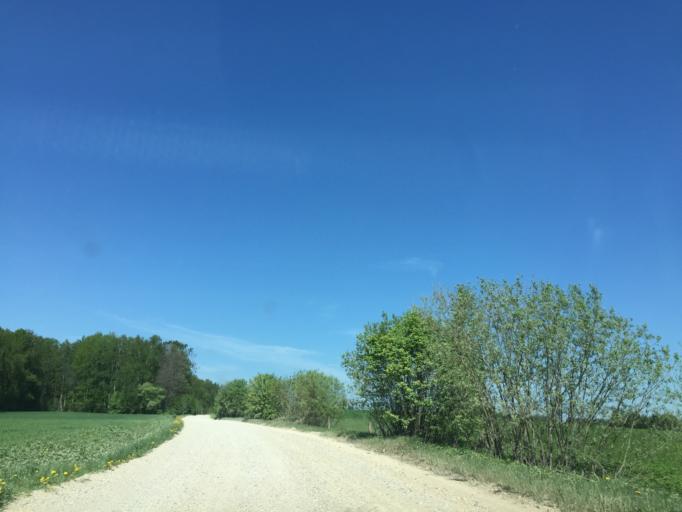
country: LV
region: Ikskile
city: Ikskile
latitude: 56.8748
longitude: 24.4981
